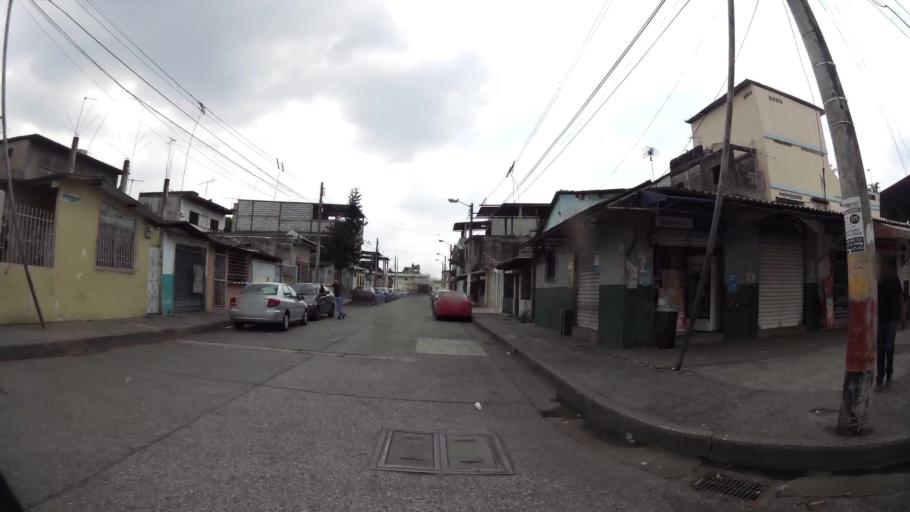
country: EC
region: Guayas
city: Guayaquil
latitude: -2.2297
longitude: -79.9032
